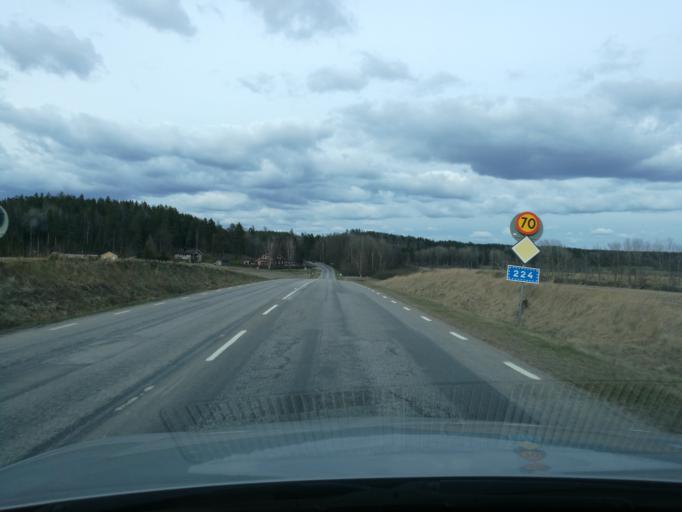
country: SE
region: Soedermanland
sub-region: Gnesta Kommun
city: Gnesta
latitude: 58.9025
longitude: 17.3164
